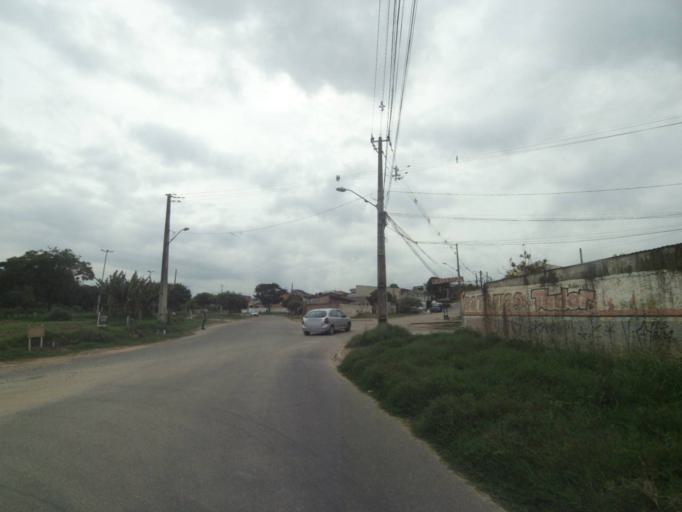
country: BR
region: Parana
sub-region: Sao Jose Dos Pinhais
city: Sao Jose dos Pinhais
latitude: -25.5536
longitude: -49.2670
